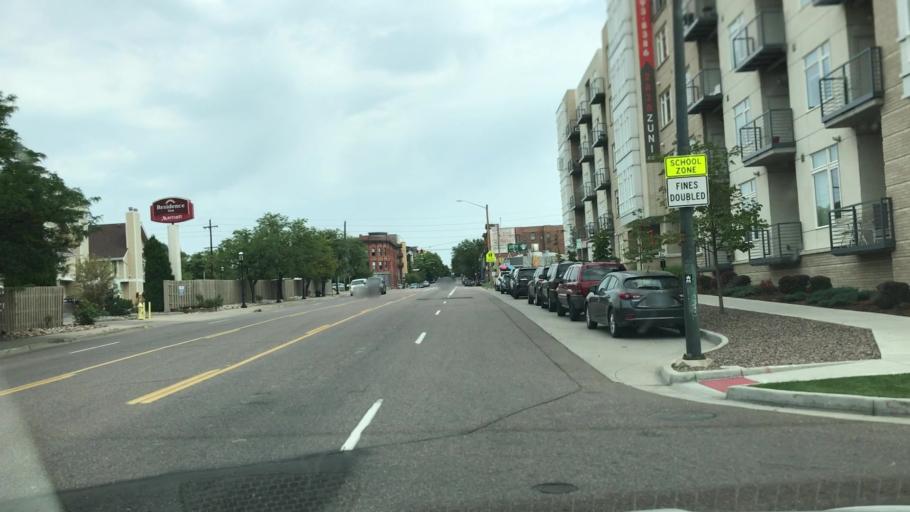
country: US
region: Colorado
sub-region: Denver County
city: Denver
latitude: 39.7572
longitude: -105.0158
